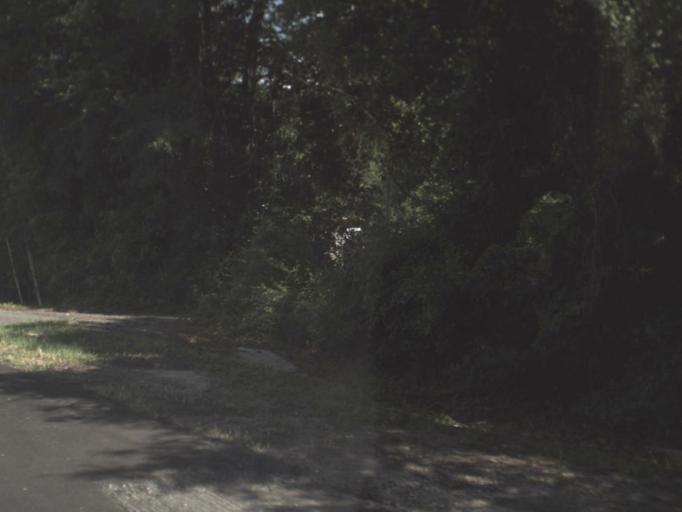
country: US
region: Florida
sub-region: Alachua County
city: Alachua
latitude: 29.7804
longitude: -82.4540
